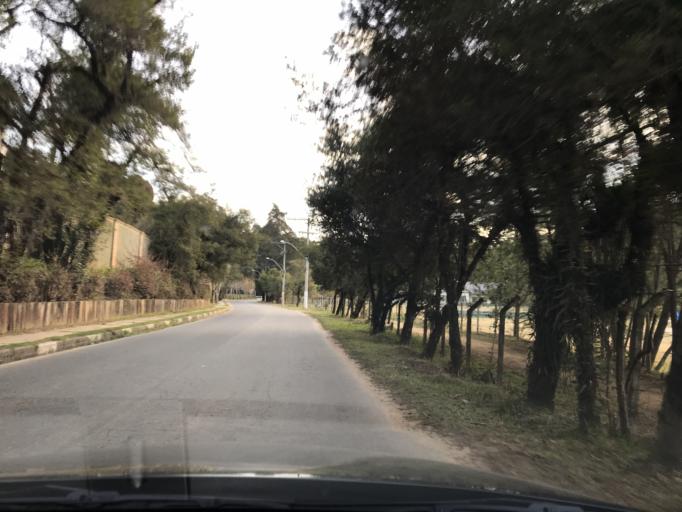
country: BR
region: Sao Paulo
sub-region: Campos Do Jordao
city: Campos do Jordao
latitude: -22.7088
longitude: -45.5465
